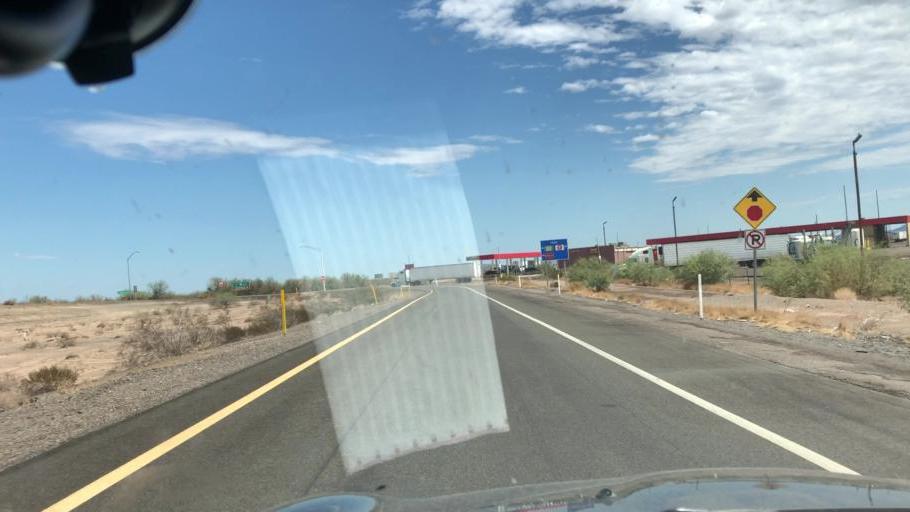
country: US
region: Arizona
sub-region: La Paz County
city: Salome
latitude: 33.6297
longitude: -113.7689
